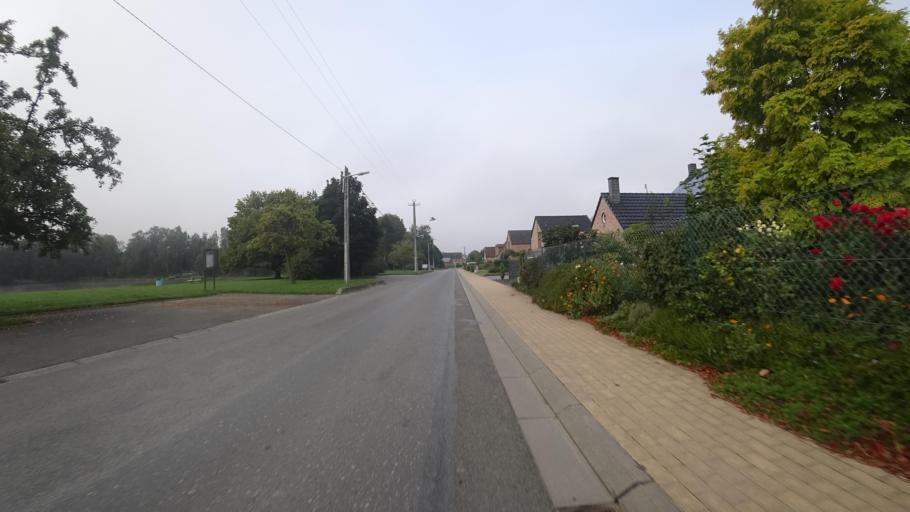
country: BE
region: Wallonia
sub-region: Province du Brabant Wallon
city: Perwez
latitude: 50.5859
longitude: 4.7795
